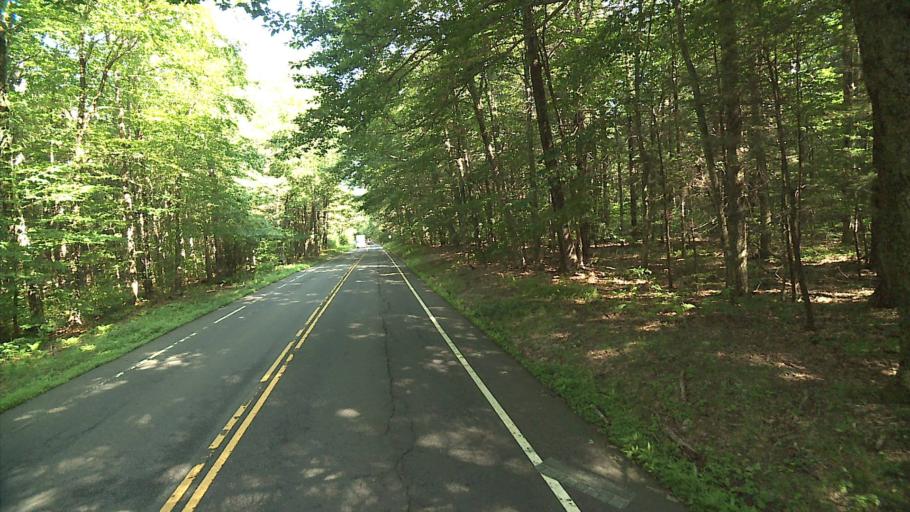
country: US
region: Massachusetts
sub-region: Hampden County
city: Granville
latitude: 42.0246
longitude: -72.9545
